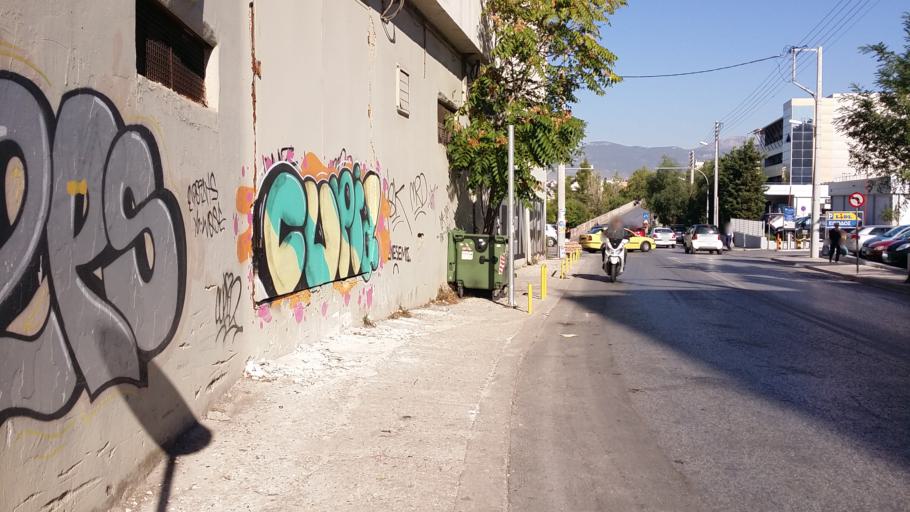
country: GR
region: Attica
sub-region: Nomarchia Athinas
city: Nea Ionia
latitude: 38.0427
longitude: 23.7606
